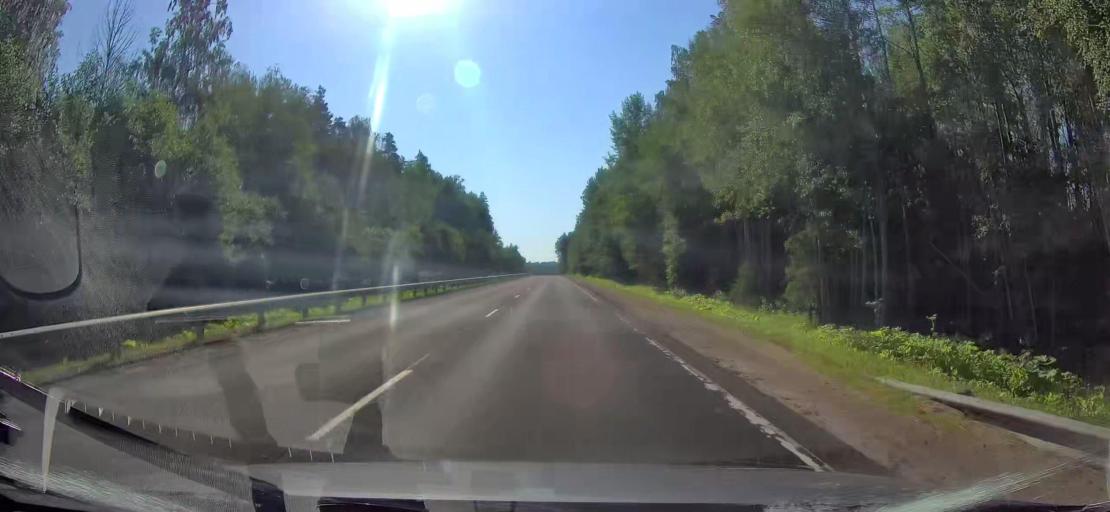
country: RU
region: Leningrad
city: Khvalovo
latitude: 59.8799
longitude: 32.8525
